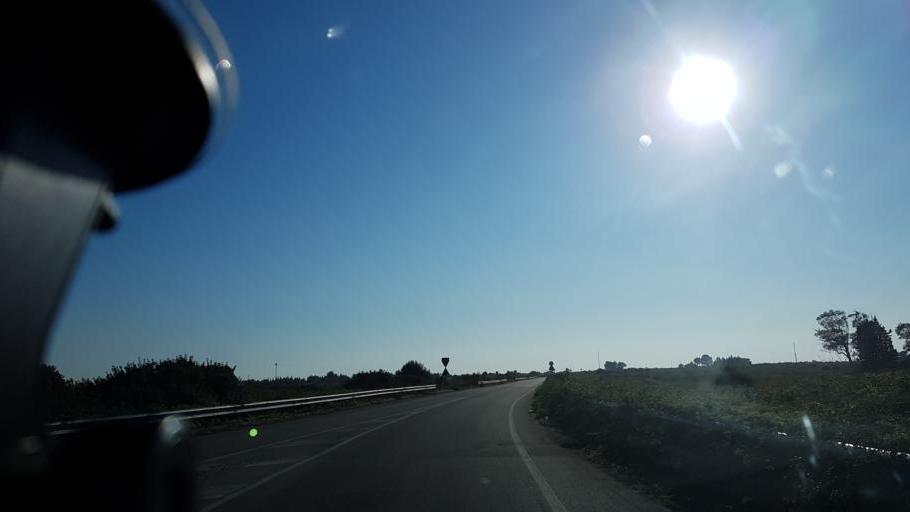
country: IT
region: Apulia
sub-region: Provincia di Lecce
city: Merine
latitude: 40.4089
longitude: 18.2575
